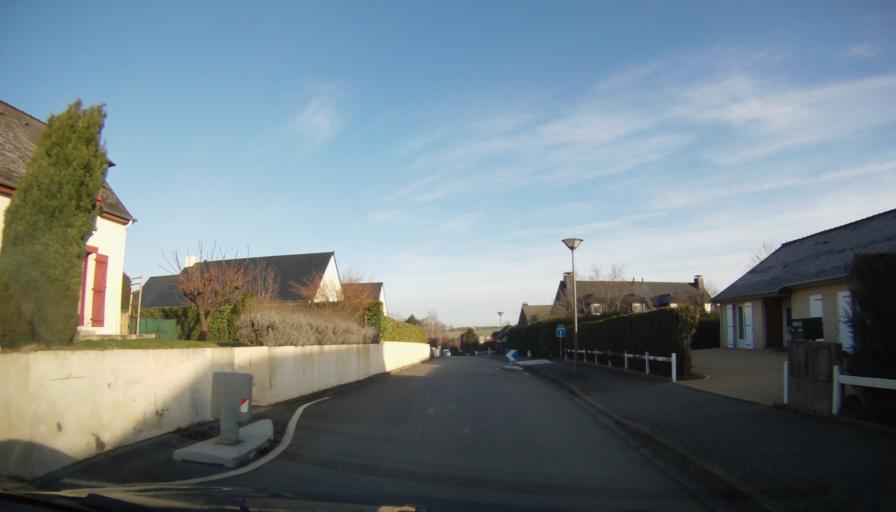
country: FR
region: Brittany
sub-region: Departement d'Ille-et-Vilaine
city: Bourgbarre
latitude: 47.9945
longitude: -1.6129
